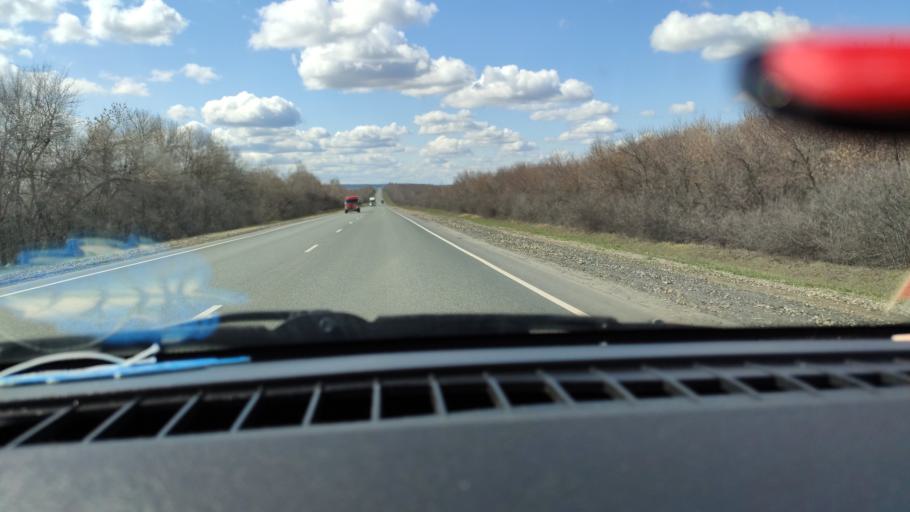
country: RU
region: Saratov
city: Khvalynsk
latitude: 52.6094
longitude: 48.1567
